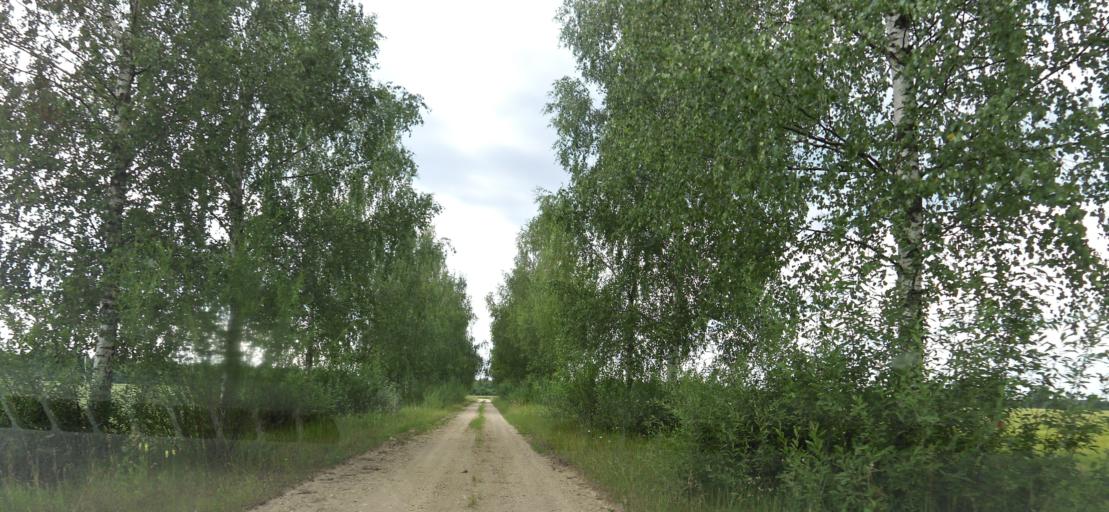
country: LT
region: Panevezys
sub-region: Birzai
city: Birzai
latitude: 56.3605
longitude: 24.9507
